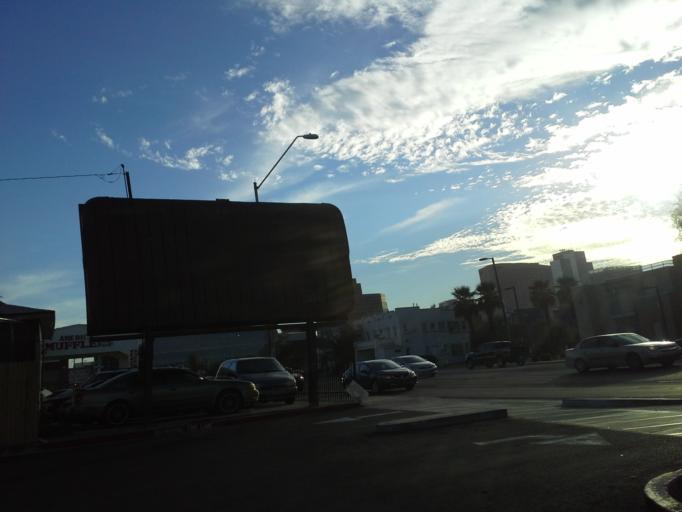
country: US
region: Arizona
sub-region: Maricopa County
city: Phoenix
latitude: 33.4582
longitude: -112.0650
